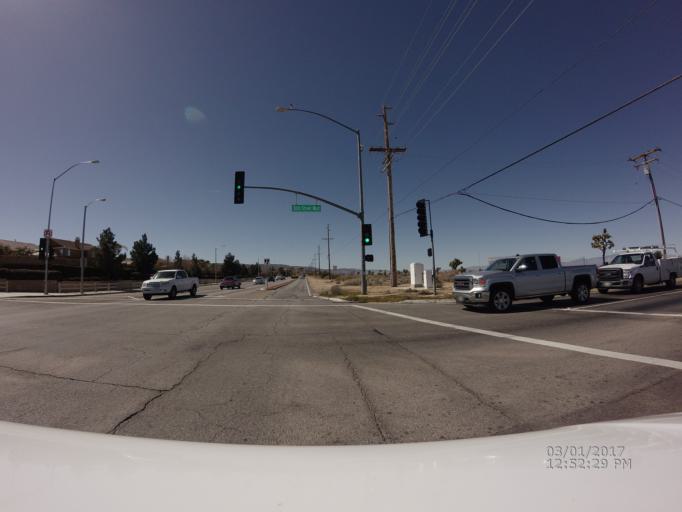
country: US
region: California
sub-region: Los Angeles County
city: Quartz Hill
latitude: 34.6457
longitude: -118.1831
